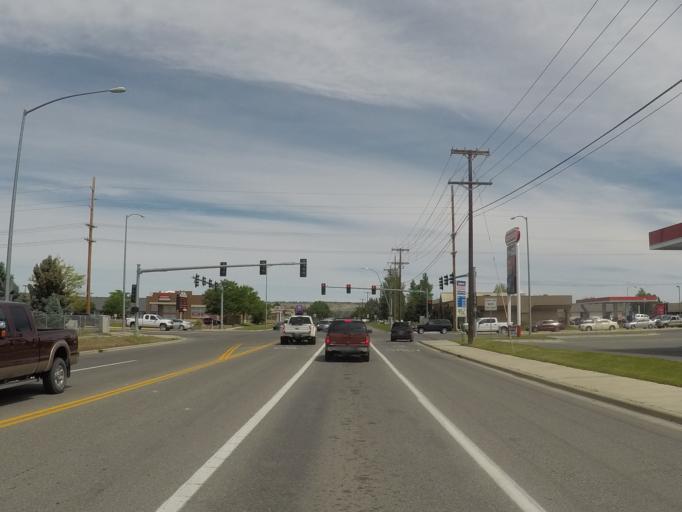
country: US
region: Montana
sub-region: Yellowstone County
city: Billings
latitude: 45.7545
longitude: -108.5968
